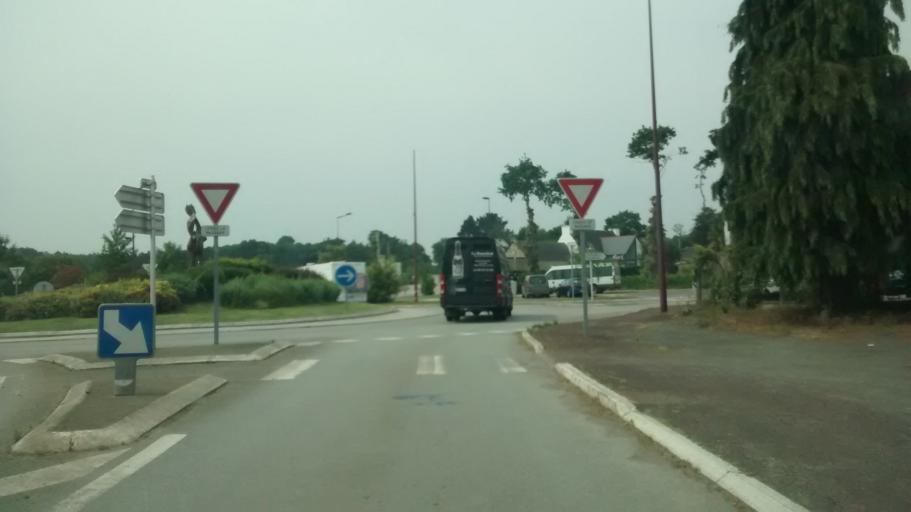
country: FR
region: Brittany
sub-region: Departement du Morbihan
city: Ruffiac
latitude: 47.8609
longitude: -2.2365
